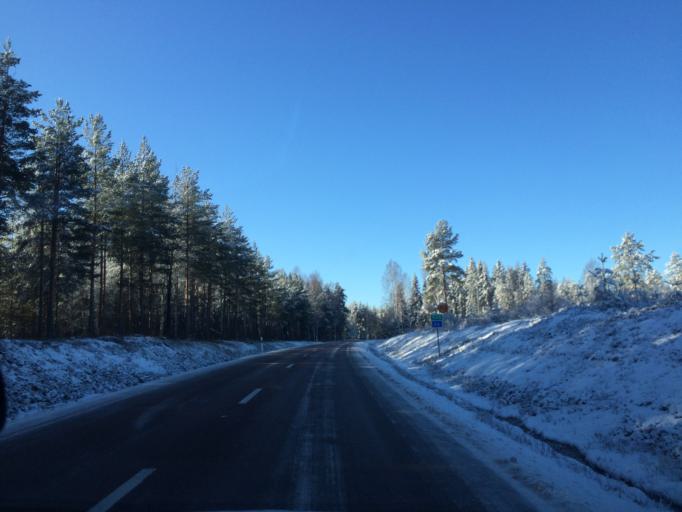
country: SE
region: Dalarna
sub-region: Mora Kommun
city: Mora
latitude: 60.9250
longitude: 14.4717
